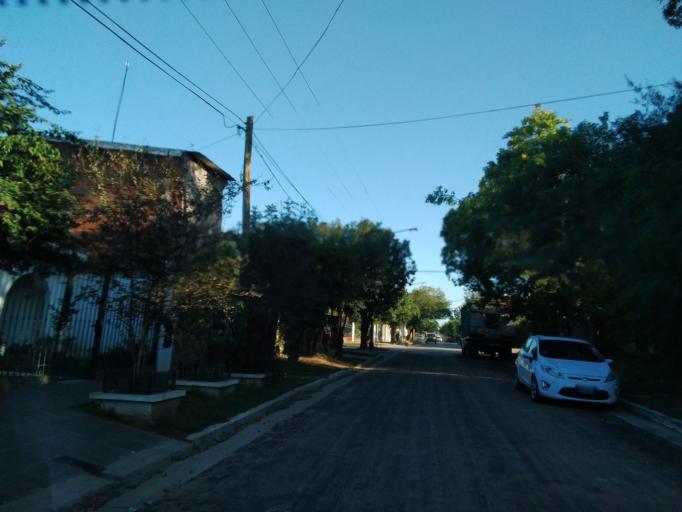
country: AR
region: Corrientes
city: Corrientes
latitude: -27.5038
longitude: -58.8046
